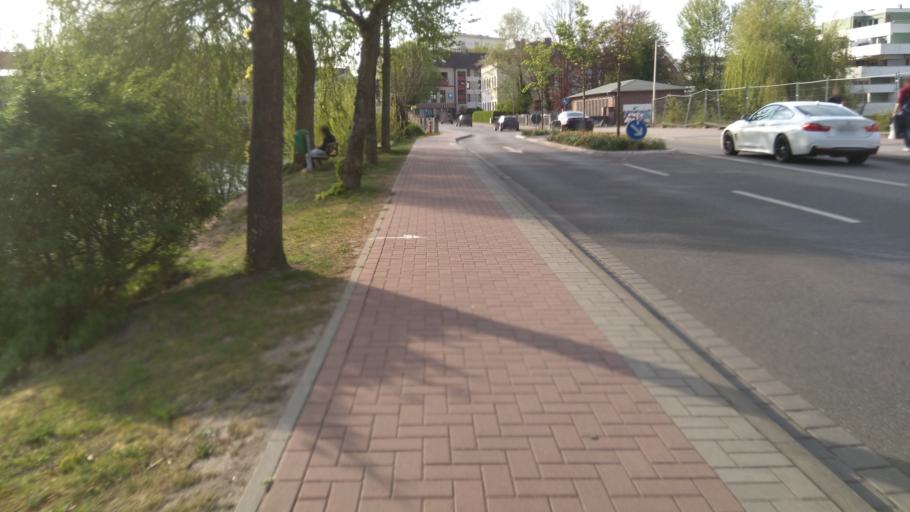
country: DE
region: Lower Saxony
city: Buxtehude
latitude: 53.4645
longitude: 9.6922
